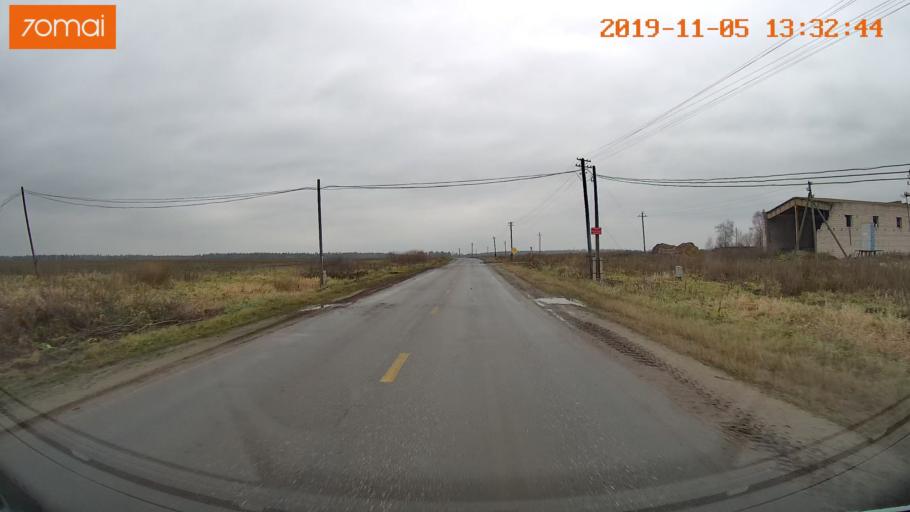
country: RU
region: Ivanovo
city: Shuya
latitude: 56.8858
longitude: 41.3968
